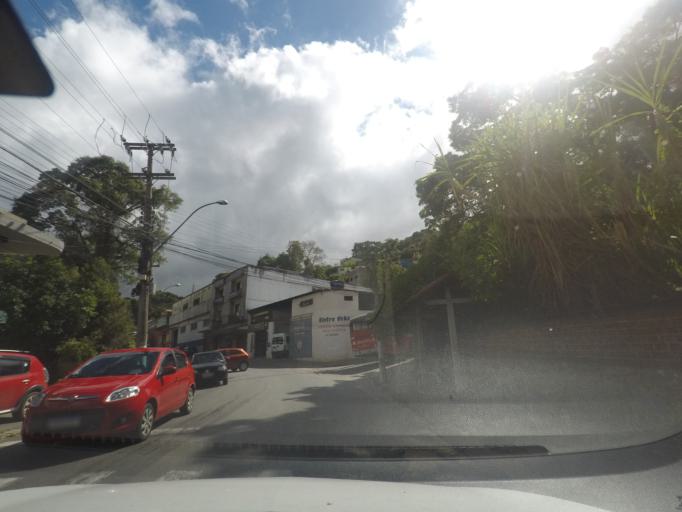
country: BR
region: Rio de Janeiro
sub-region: Teresopolis
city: Teresopolis
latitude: -22.3997
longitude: -42.9612
